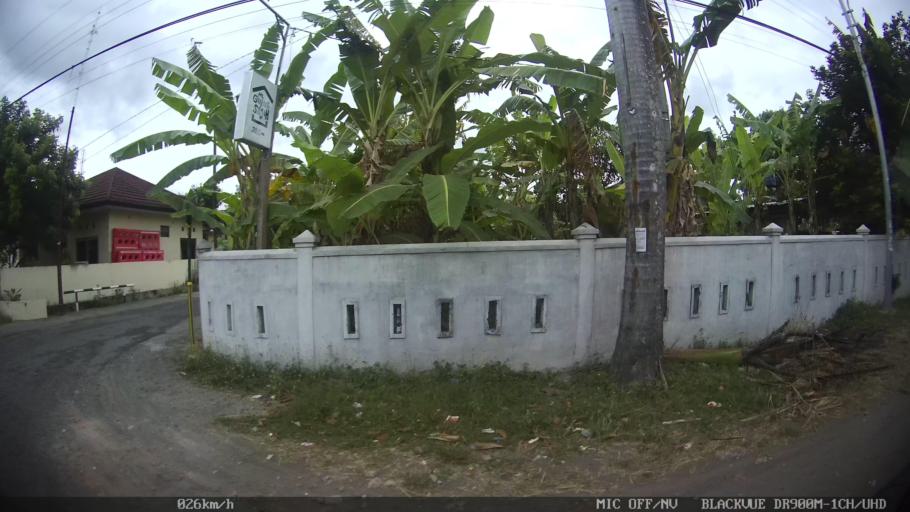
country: ID
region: Daerah Istimewa Yogyakarta
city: Sewon
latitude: -7.8658
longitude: 110.4046
